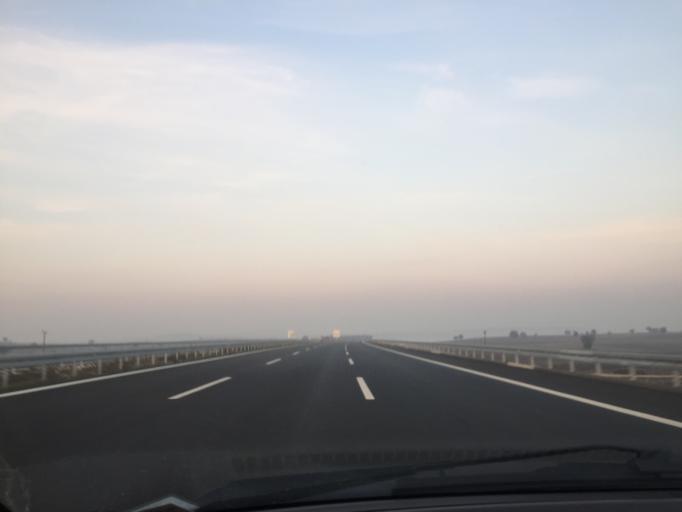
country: TR
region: Bursa
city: Mahmudiye
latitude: 40.2571
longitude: 28.6950
